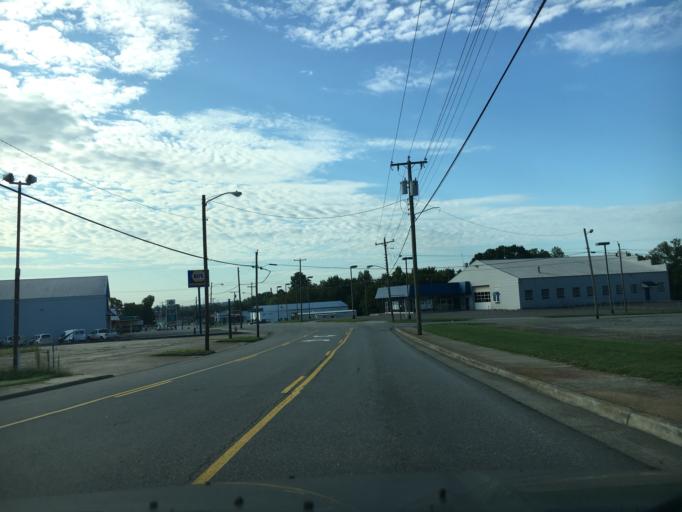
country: US
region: Virginia
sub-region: Halifax County
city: South Boston
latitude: 36.7058
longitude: -78.9097
